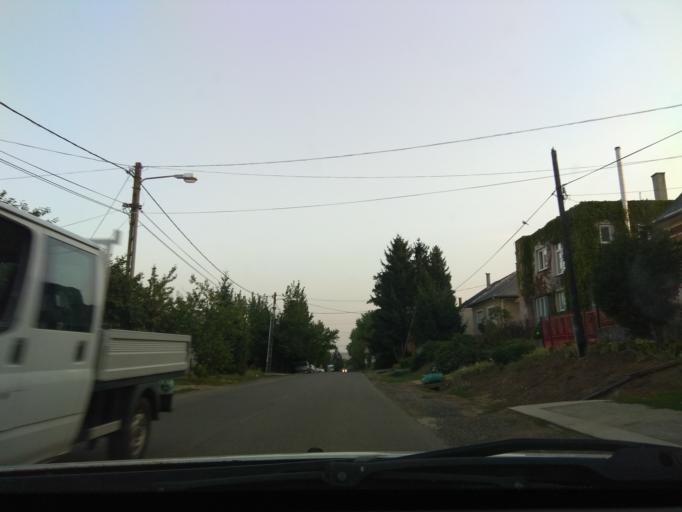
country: HU
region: Borsod-Abauj-Zemplen
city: Szerencs
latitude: 48.1715
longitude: 21.2040
